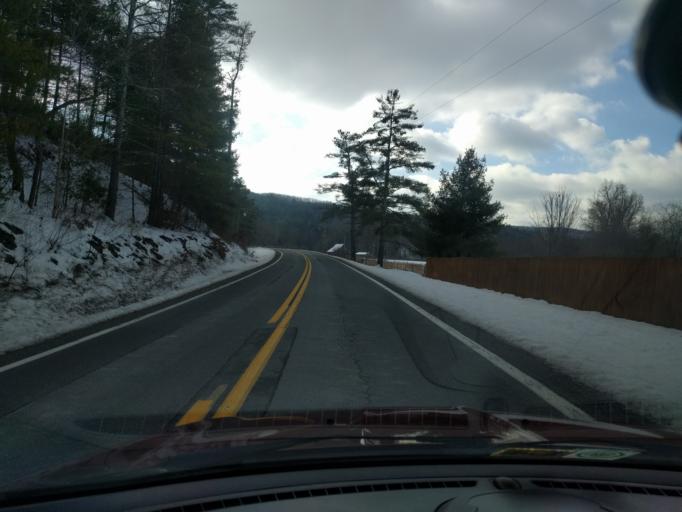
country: US
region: West Virginia
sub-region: Pocahontas County
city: Marlinton
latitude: 38.1499
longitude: -79.9832
